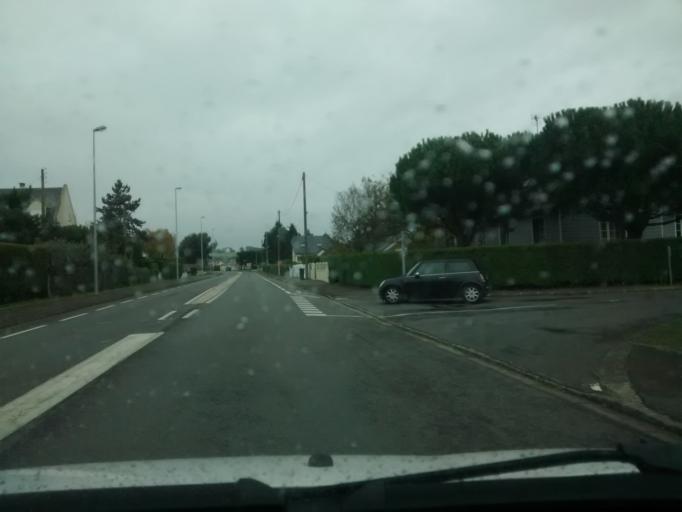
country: FR
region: Lower Normandy
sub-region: Departement de la Manche
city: Saint-Pair-sur-Mer
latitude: 48.7979
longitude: -1.5658
